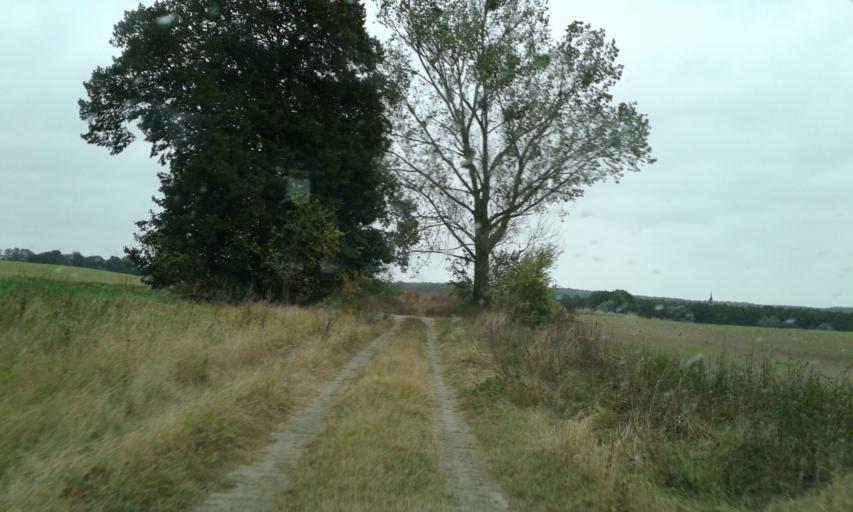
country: PL
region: West Pomeranian Voivodeship
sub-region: Powiat stargardzki
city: Dolice
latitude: 53.1091
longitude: 15.2227
